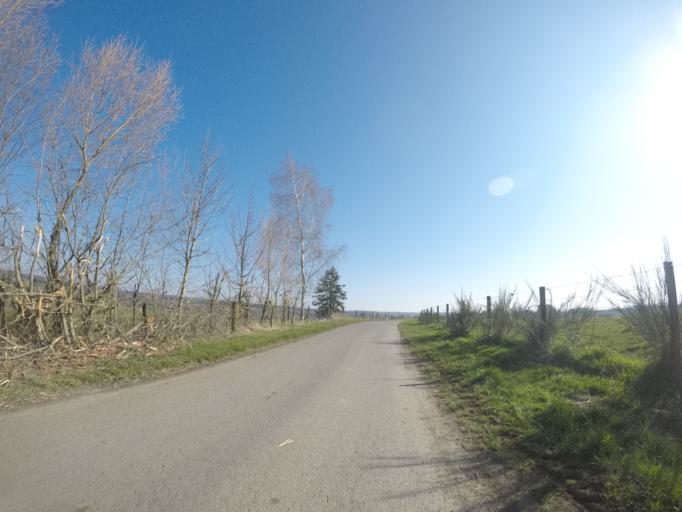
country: BE
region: Wallonia
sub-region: Province du Luxembourg
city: Etalle
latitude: 49.7126
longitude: 5.5743
